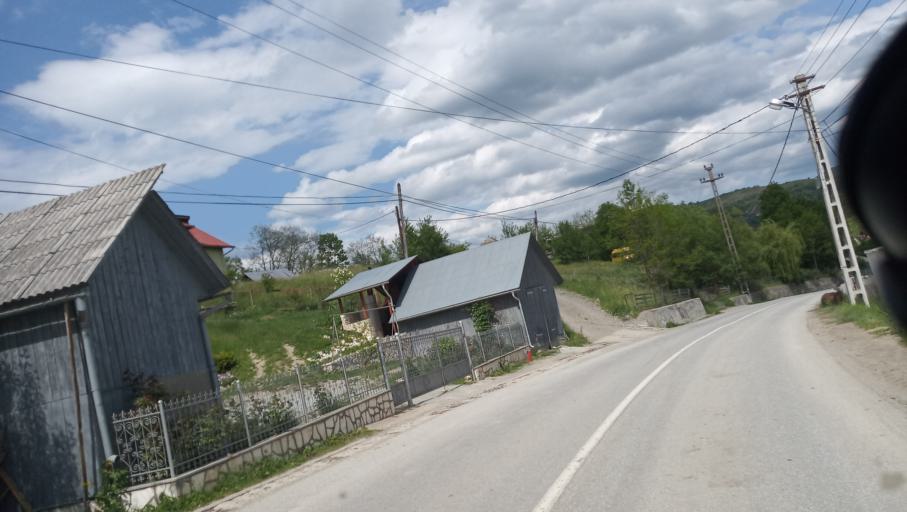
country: RO
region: Alba
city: Abrud
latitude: 46.2711
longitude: 23.0483
